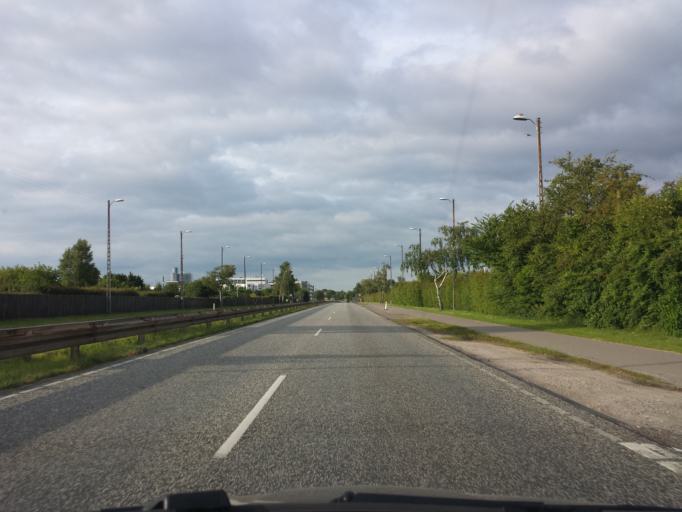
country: DK
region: Capital Region
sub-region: Herlev Kommune
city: Herlev
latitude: 55.7102
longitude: 12.4319
